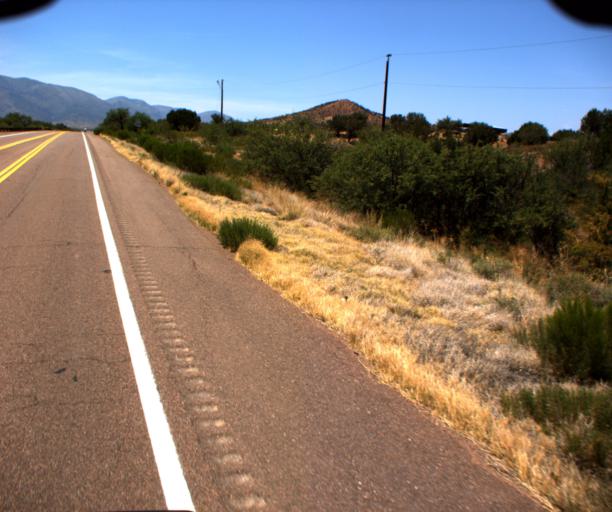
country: US
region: Arizona
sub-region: Gila County
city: Tonto Basin
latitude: 34.0120
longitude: -111.3217
